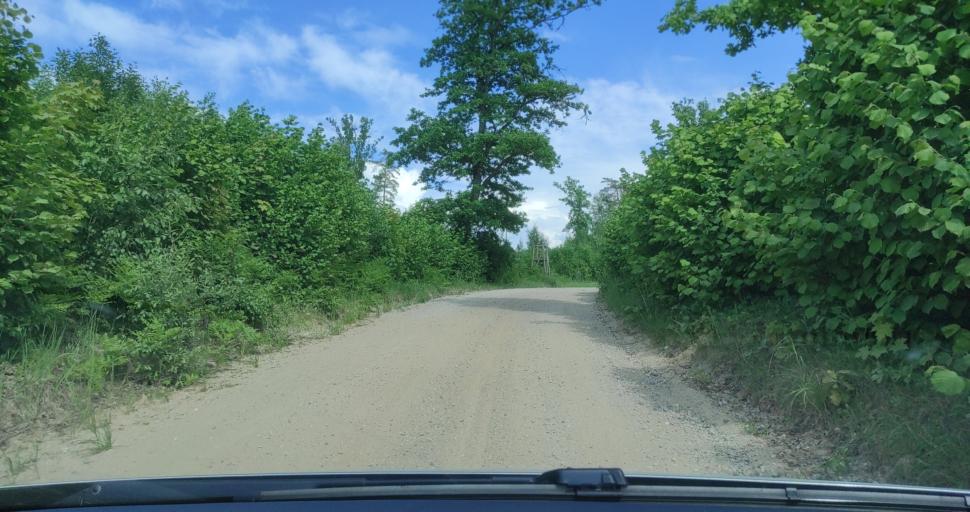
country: LV
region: Kuldigas Rajons
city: Kuldiga
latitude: 56.8596
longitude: 21.9213
